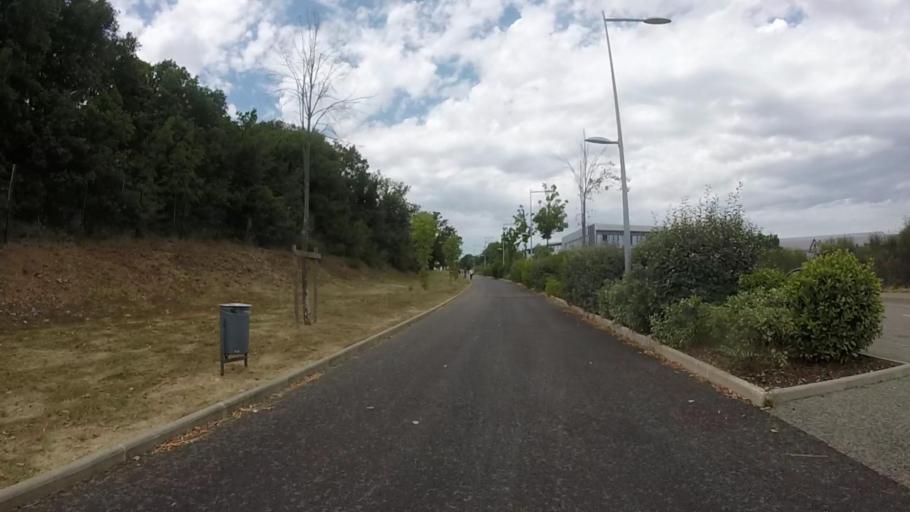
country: FR
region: Provence-Alpes-Cote d'Azur
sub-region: Departement des Alpes-Maritimes
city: Biot
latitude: 43.6225
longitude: 7.0726
